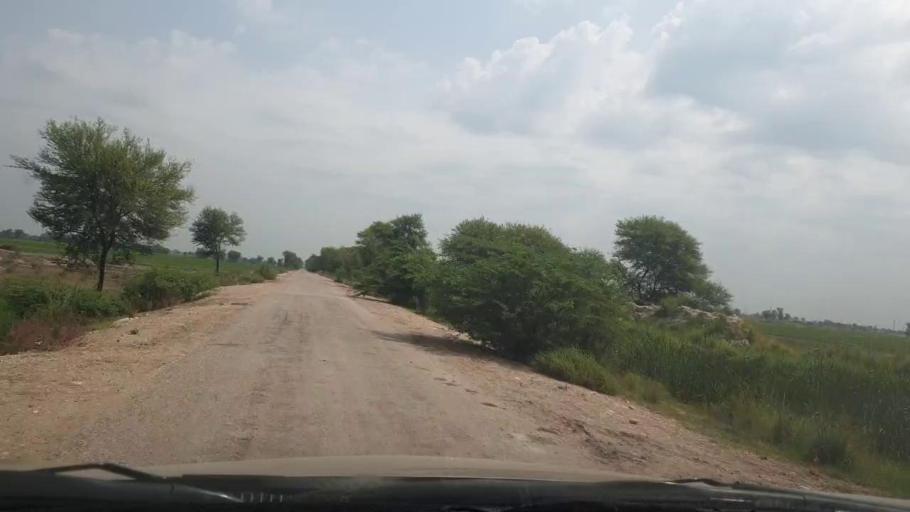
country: PK
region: Sindh
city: Miro Khan
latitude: 27.6883
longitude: 68.1928
